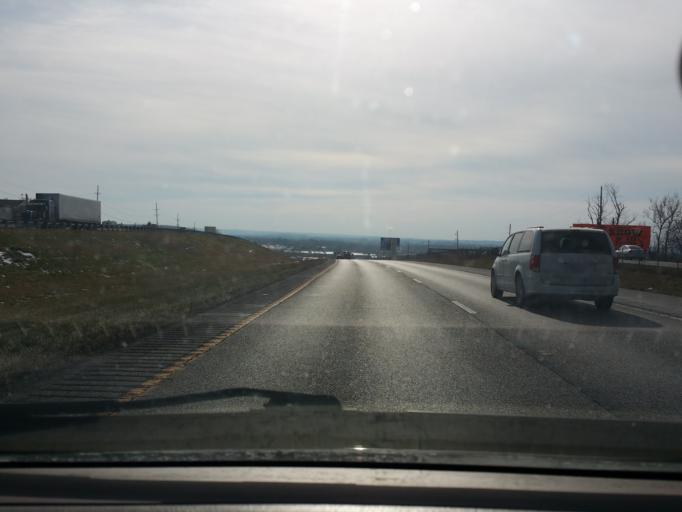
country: US
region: Missouri
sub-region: Clay County
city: Liberty
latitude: 39.2592
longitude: -94.4497
